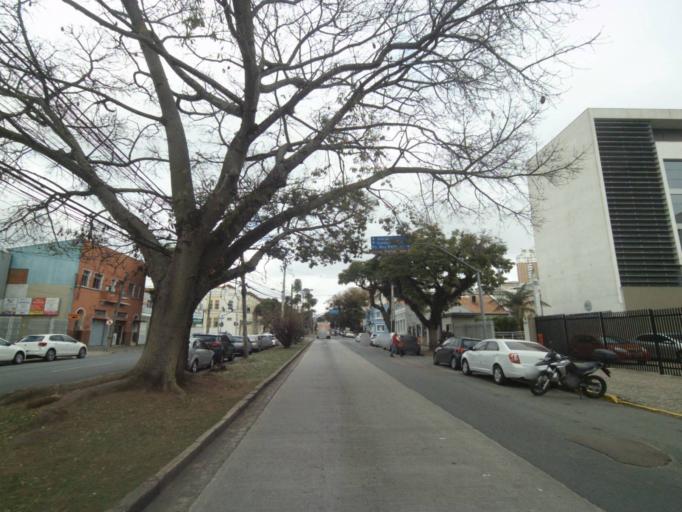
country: BR
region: Parana
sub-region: Curitiba
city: Curitiba
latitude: -25.4424
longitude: -49.2699
